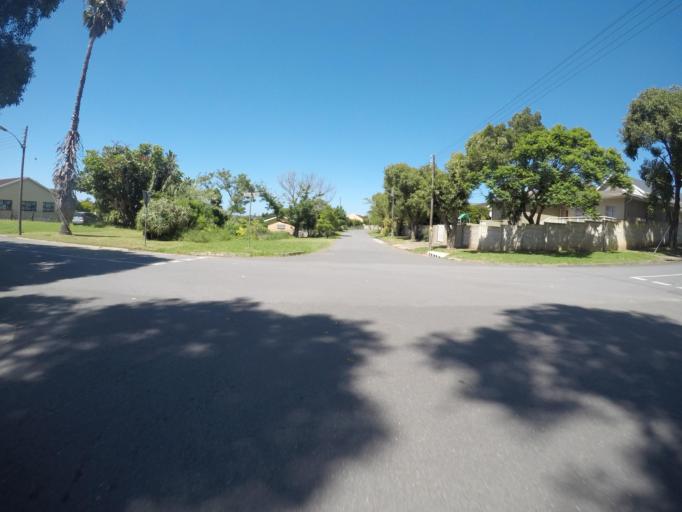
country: ZA
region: Eastern Cape
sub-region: Buffalo City Metropolitan Municipality
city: East London
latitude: -32.9695
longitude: 27.9461
